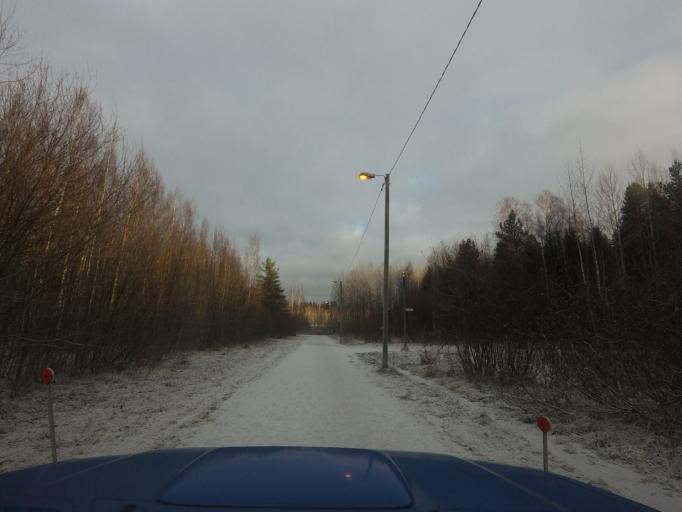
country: FI
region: Uusimaa
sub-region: Helsinki
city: Kauniainen
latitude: 60.2048
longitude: 24.6992
